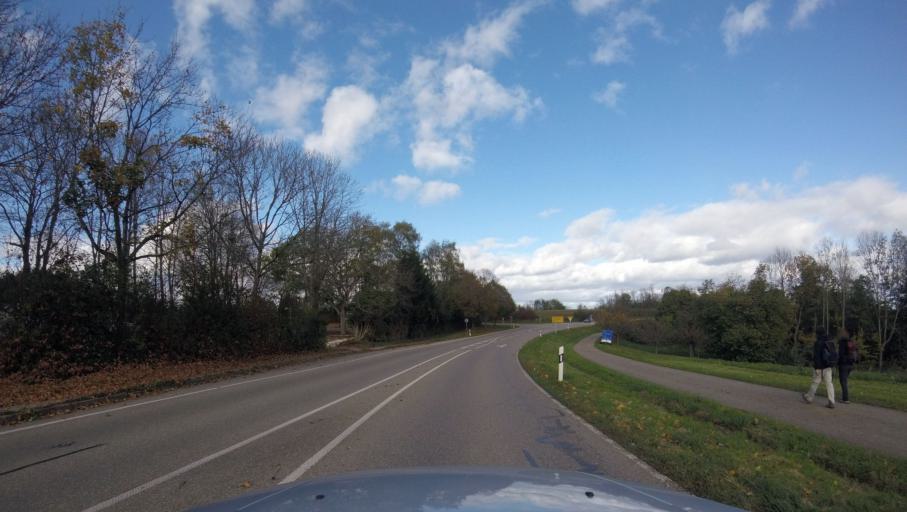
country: DE
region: Baden-Wuerttemberg
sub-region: Regierungsbezirk Stuttgart
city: Ottenbach
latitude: 48.7472
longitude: 9.7227
